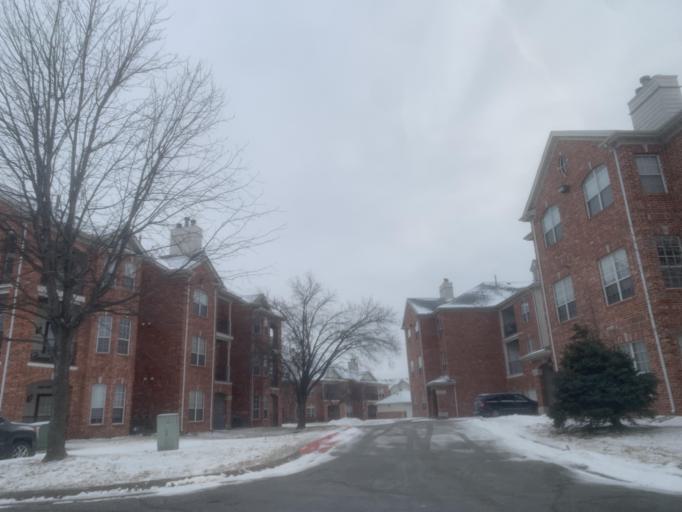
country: US
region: Nebraska
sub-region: Douglas County
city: Ralston
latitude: 41.2739
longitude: -96.0894
